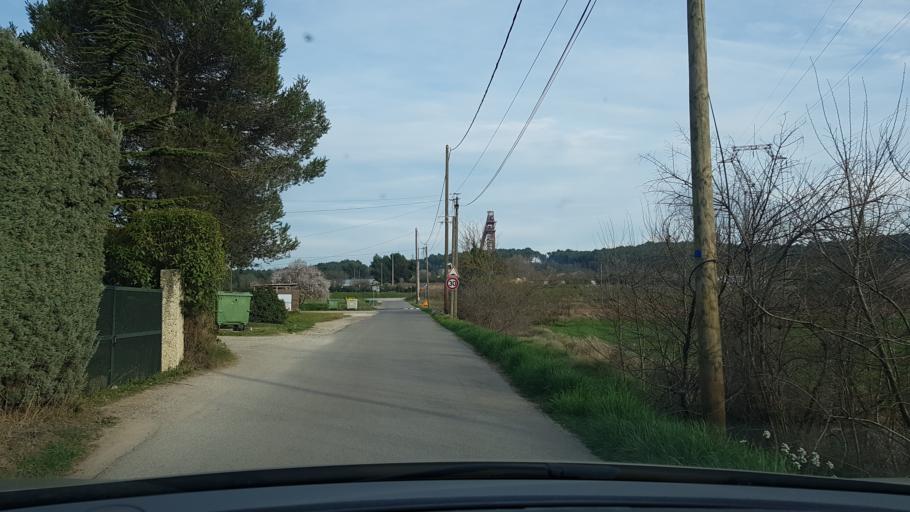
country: FR
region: Provence-Alpes-Cote d'Azur
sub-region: Departement des Bouches-du-Rhone
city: Gardanne
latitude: 43.4702
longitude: 5.4668
